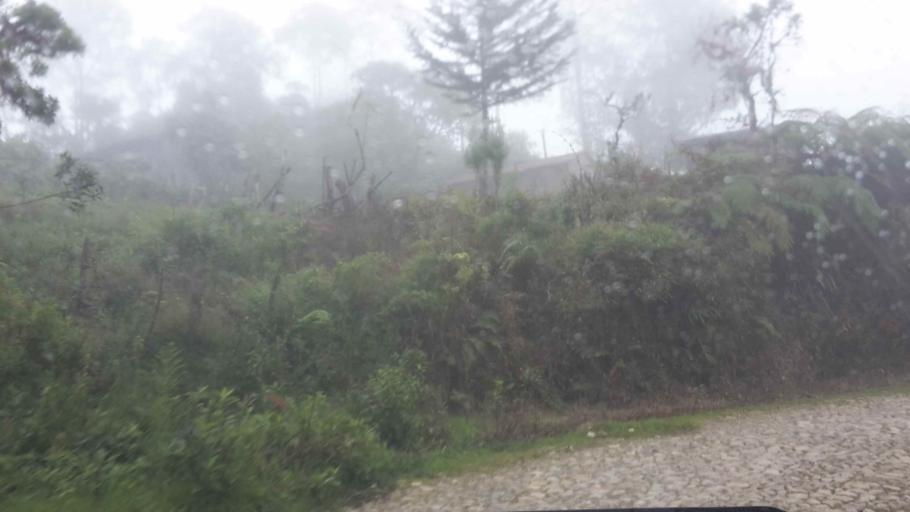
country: BO
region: Cochabamba
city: Colomi
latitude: -17.1293
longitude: -65.9654
